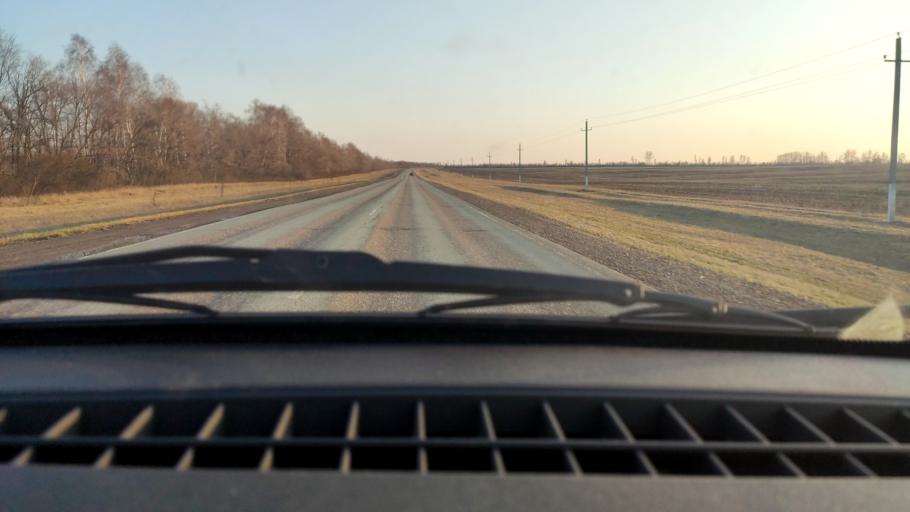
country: RU
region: Bashkortostan
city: Davlekanovo
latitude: 54.3377
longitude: 55.1701
